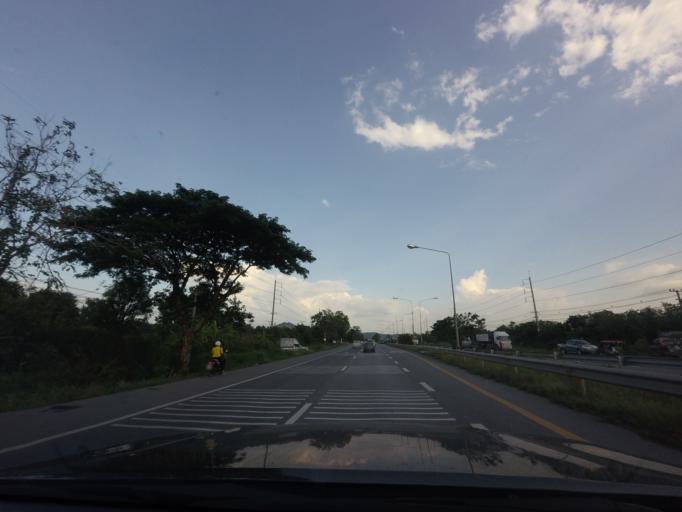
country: TH
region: Sara Buri
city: Saraburi
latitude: 14.5115
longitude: 100.9027
